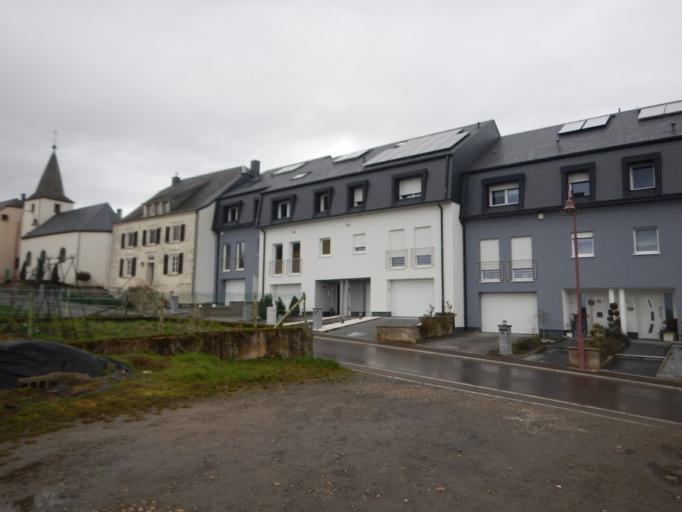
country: BE
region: Wallonia
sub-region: Province du Luxembourg
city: Attert
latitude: 49.7788
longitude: 5.8090
